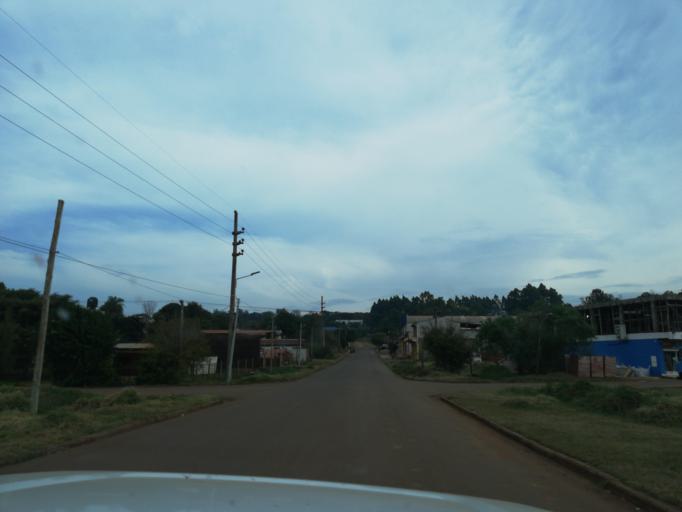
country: AR
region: Misiones
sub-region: Departamento de San Pedro
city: San Pedro
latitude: -26.6259
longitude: -54.1109
